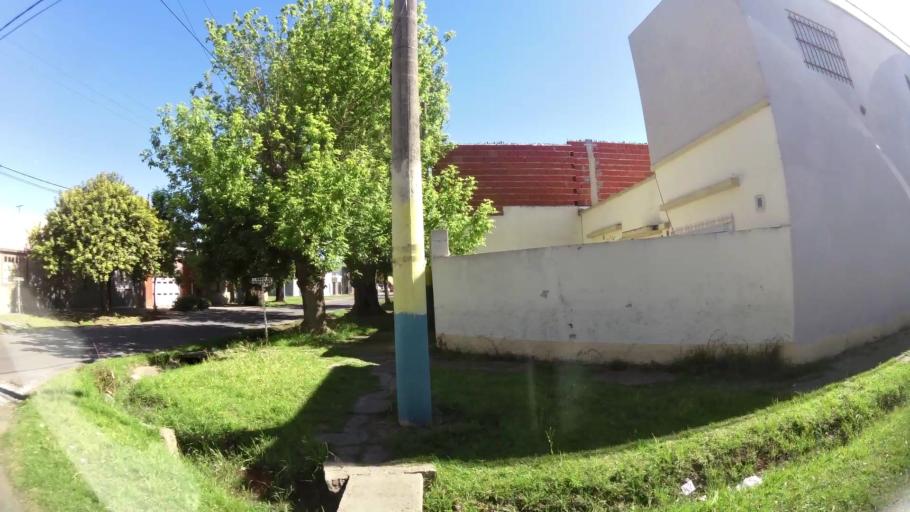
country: AR
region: Santa Fe
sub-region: Departamento de Rosario
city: Rosario
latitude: -32.9617
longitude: -60.6964
